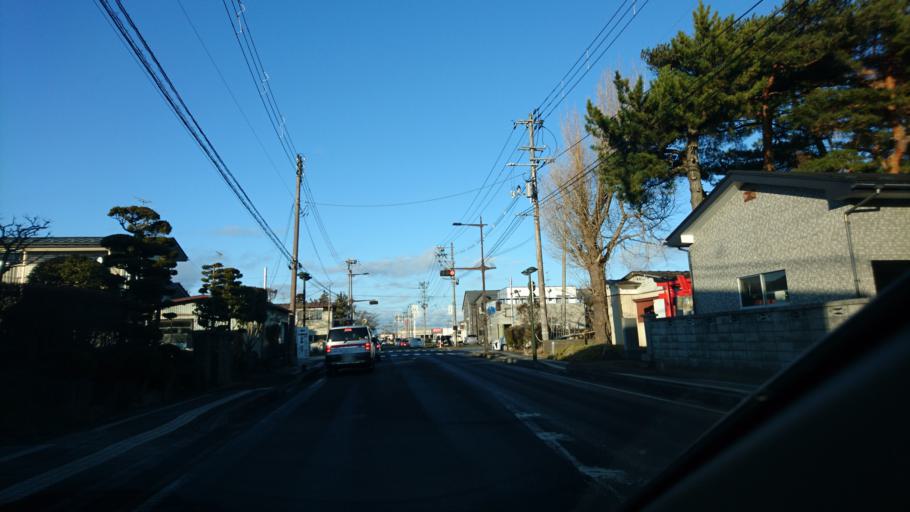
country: JP
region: Miyagi
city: Furukawa
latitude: 38.5732
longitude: 140.8598
